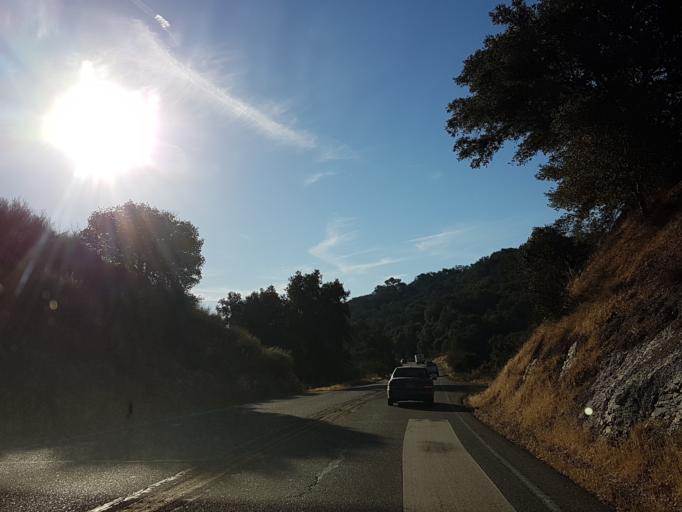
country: US
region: California
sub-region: Santa Barbara County
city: Goleta
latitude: 34.5610
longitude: -119.9194
